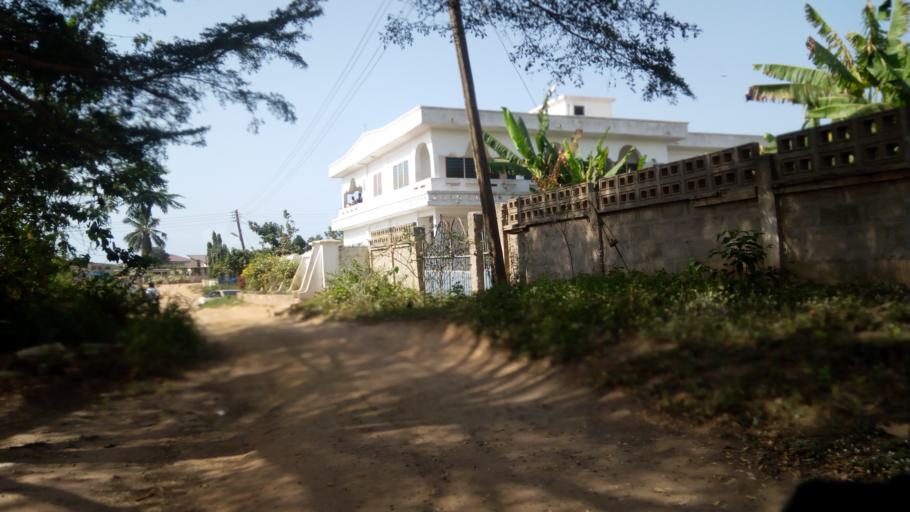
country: GH
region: Central
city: Cape Coast
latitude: 5.1203
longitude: -1.2706
